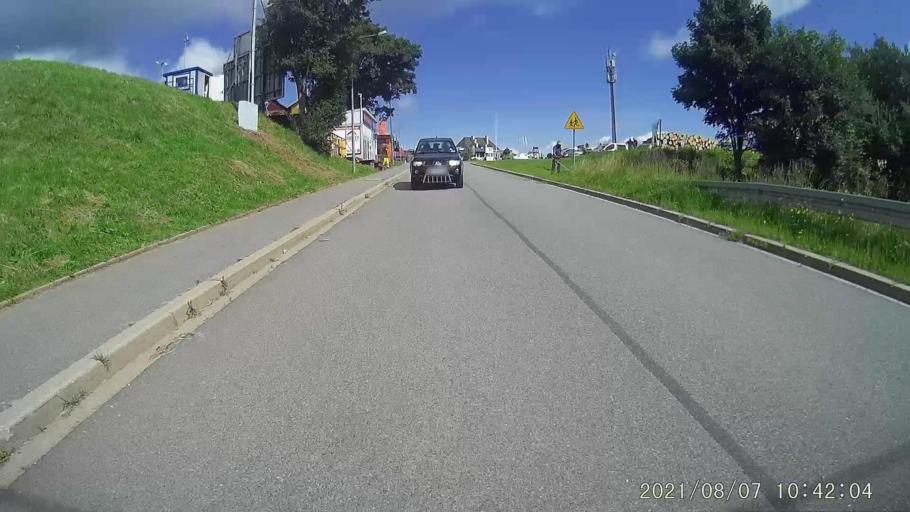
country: PL
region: Lower Silesian Voivodeship
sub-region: Powiat klodzki
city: Duszniki-Zdroj
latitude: 50.3343
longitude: 16.3892
